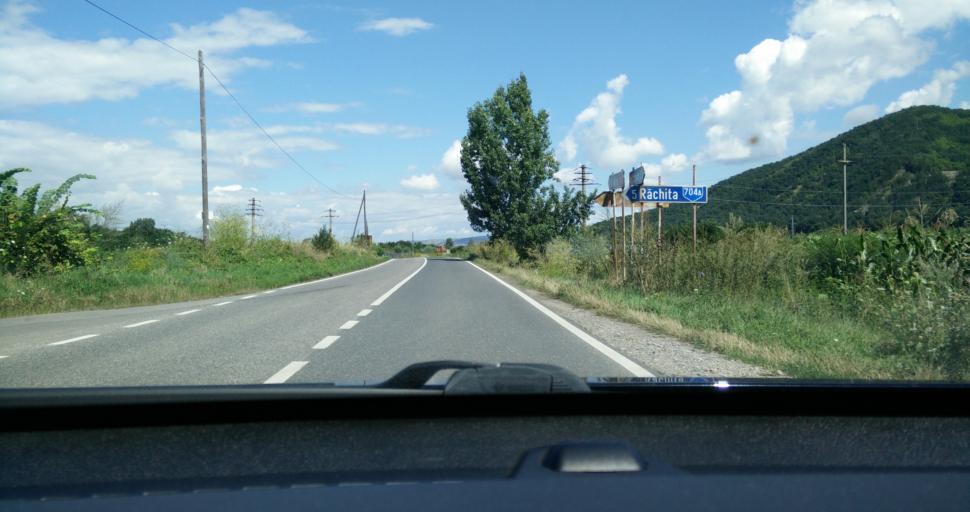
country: RO
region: Alba
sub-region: Comuna Sasciori
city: Sebesel
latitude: 45.8958
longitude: 23.5599
